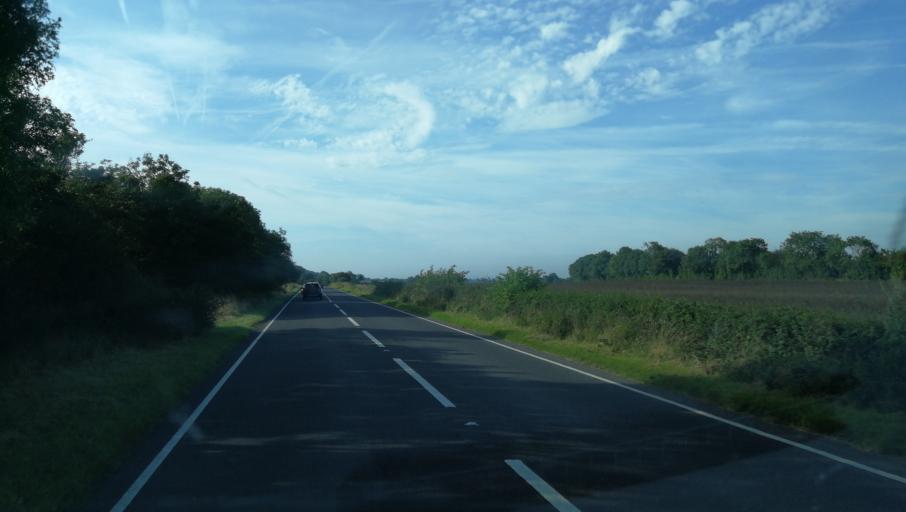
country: GB
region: England
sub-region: Oxfordshire
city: Woodstock
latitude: 51.8973
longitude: -1.3280
